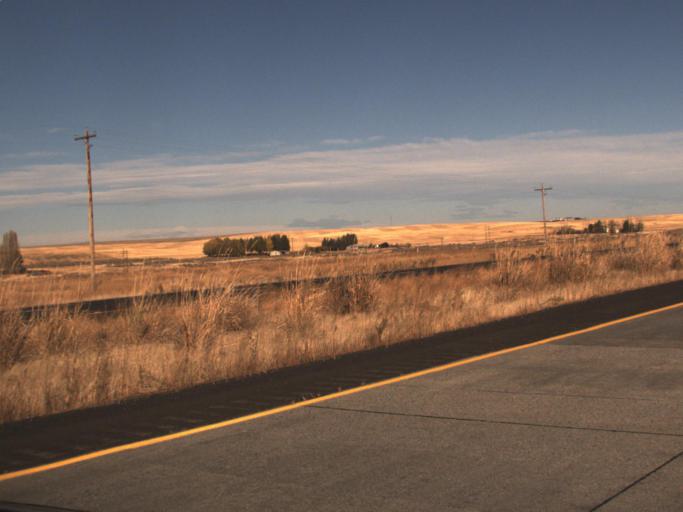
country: US
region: Washington
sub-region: Adams County
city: Ritzville
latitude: 47.0768
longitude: -118.4102
